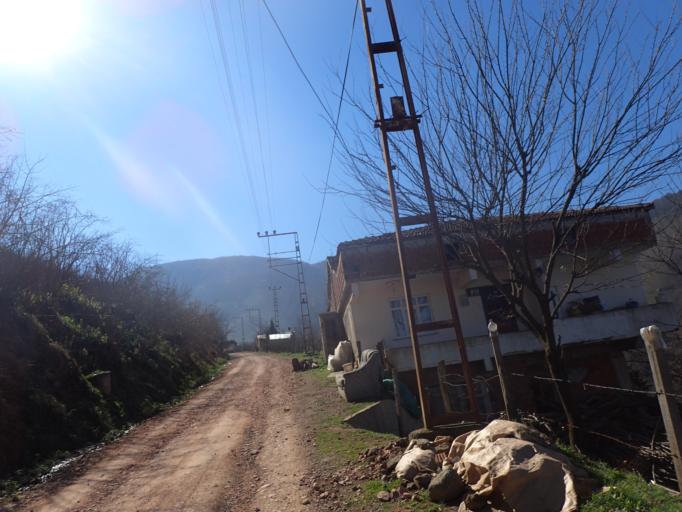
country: TR
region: Ordu
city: Catalpinar
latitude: 40.8686
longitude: 37.4927
